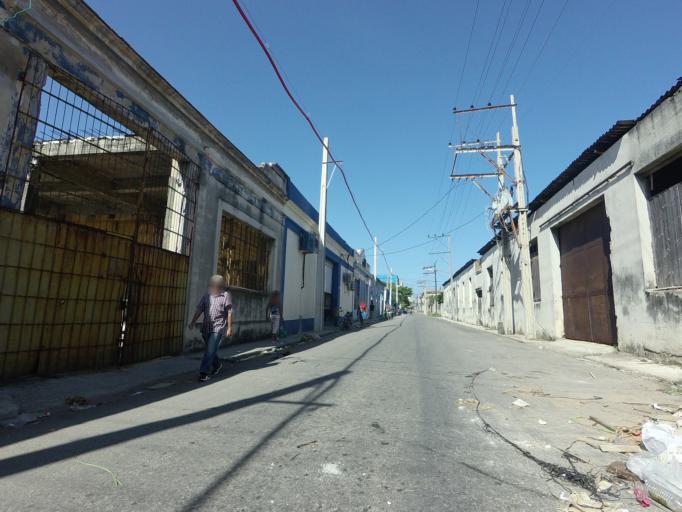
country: CU
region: La Habana
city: Havana
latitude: 23.1278
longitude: -82.3729
